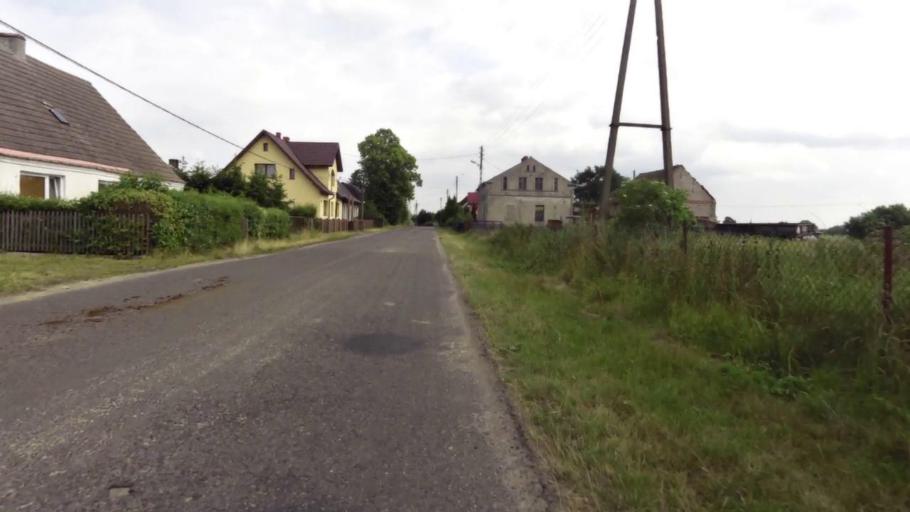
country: PL
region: West Pomeranian Voivodeship
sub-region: Powiat goleniowski
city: Stepnica
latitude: 53.6695
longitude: 14.5766
